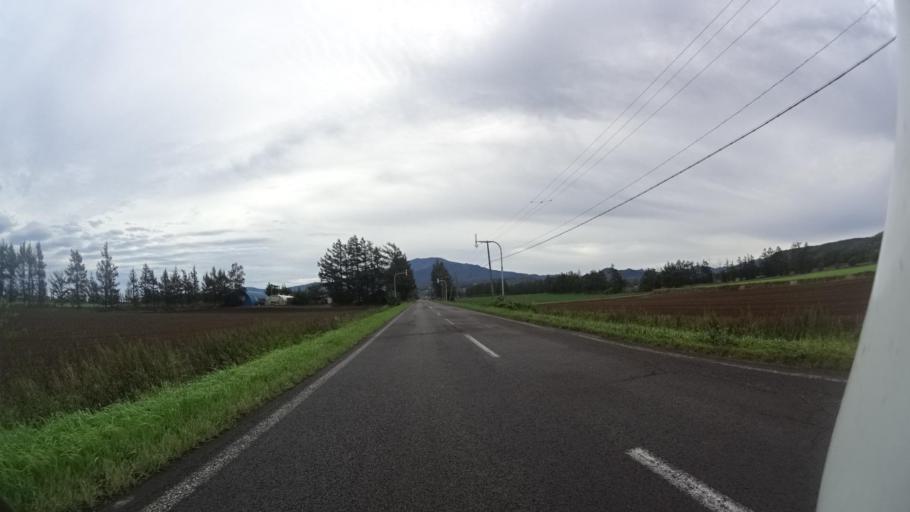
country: JP
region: Hokkaido
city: Shibetsu
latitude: 43.8736
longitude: 144.7279
